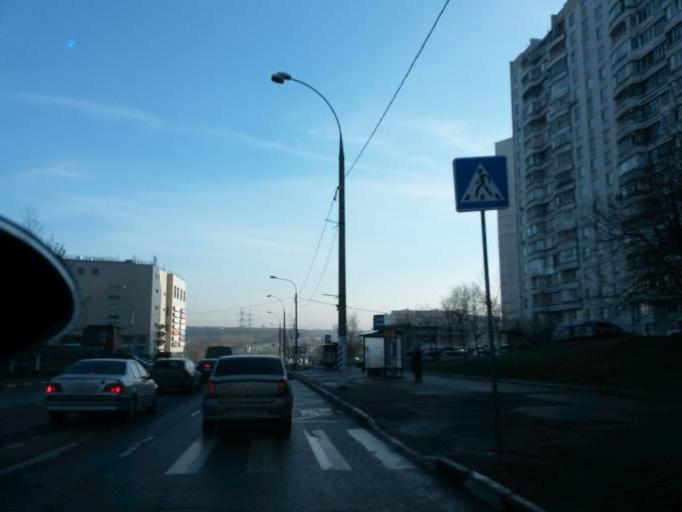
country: RU
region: Moscow
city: Chertanovo Yuzhnoye
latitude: 55.5727
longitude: 37.5652
